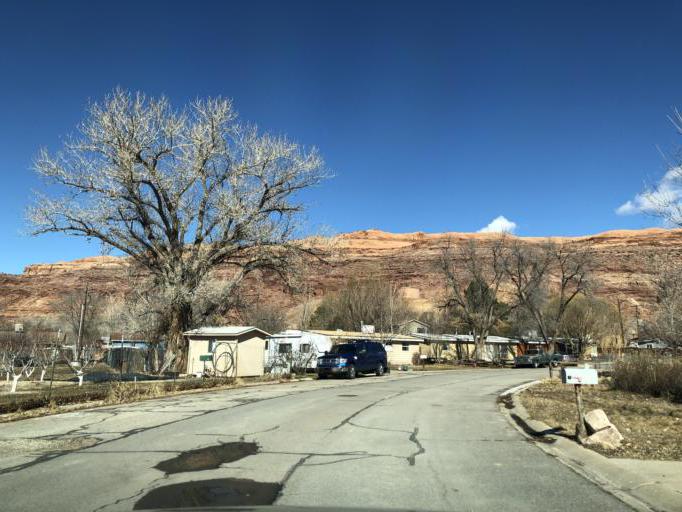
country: US
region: Utah
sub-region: Grand County
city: Moab
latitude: 38.5866
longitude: -109.5640
